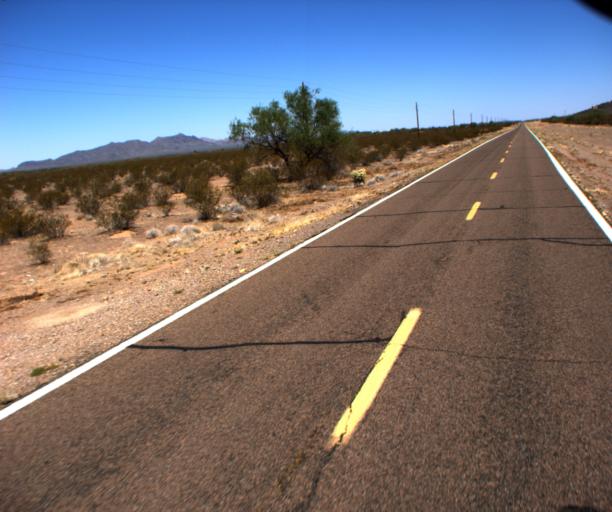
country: US
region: Arizona
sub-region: Pima County
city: Ajo
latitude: 32.2490
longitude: -112.7300
